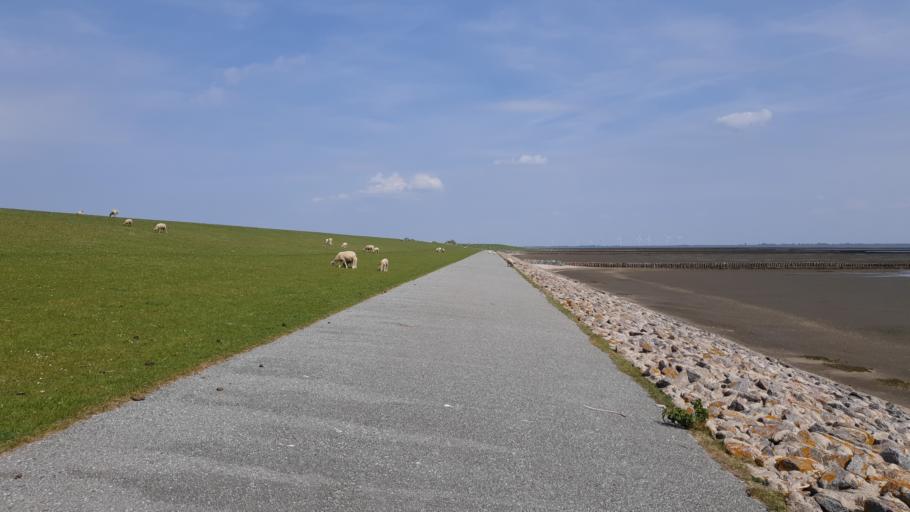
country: DE
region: Schleswig-Holstein
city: Elisabeth-Sophien-Koog
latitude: 54.4602
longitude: 8.8661
